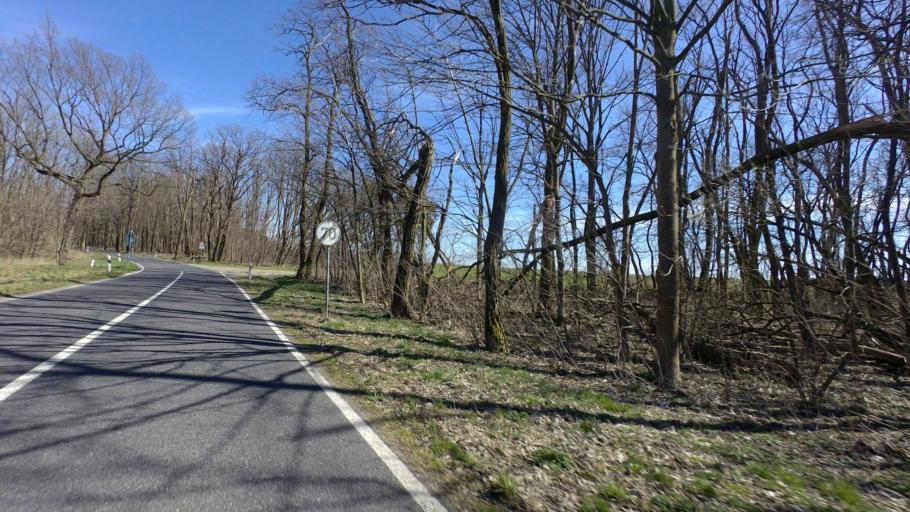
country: DE
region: Brandenburg
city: Munchehofe
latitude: 52.1553
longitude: 13.8591
